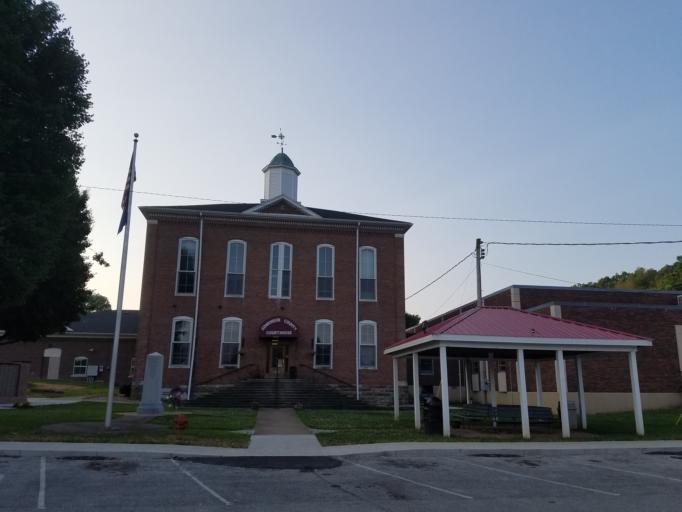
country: US
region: Kentucky
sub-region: Edmonson County
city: Brownsville
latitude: 37.1938
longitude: -86.2683
